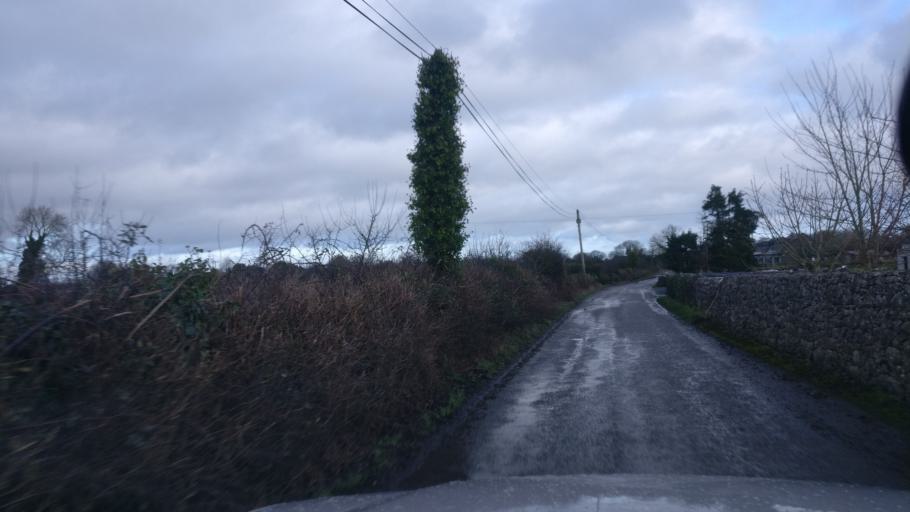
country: IE
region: Connaught
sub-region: County Galway
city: Loughrea
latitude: 53.2573
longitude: -8.6368
